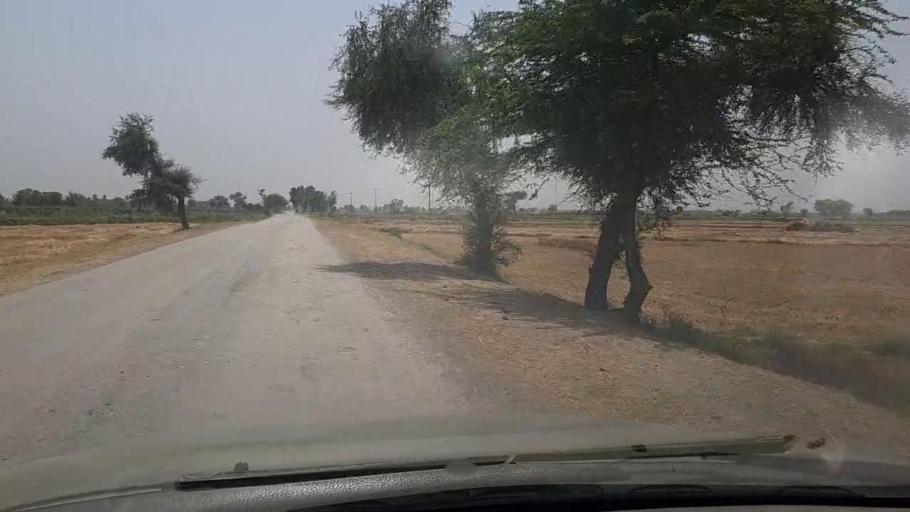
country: PK
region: Sindh
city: Miro Khan
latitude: 27.7191
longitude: 68.0682
